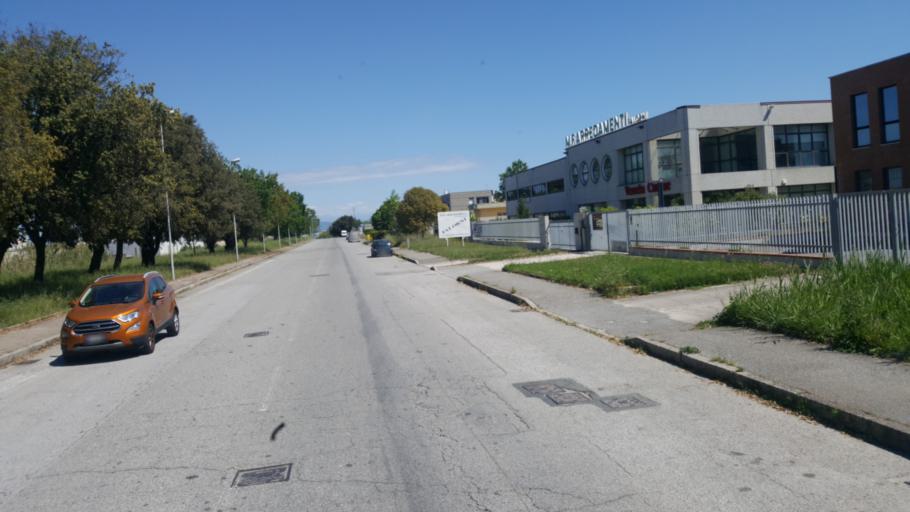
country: IT
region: Tuscany
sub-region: Provincia di Livorno
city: Livorno
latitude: 43.5717
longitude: 10.3430
